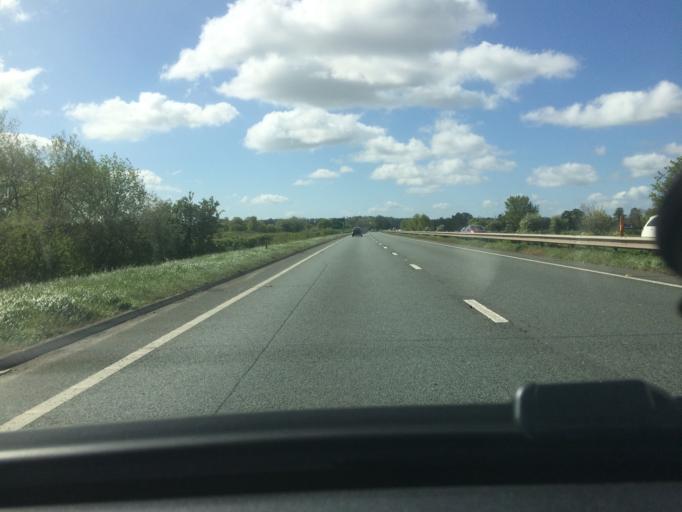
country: GB
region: Wales
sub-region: Wrexham
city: Rossett
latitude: 53.1181
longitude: -2.9509
